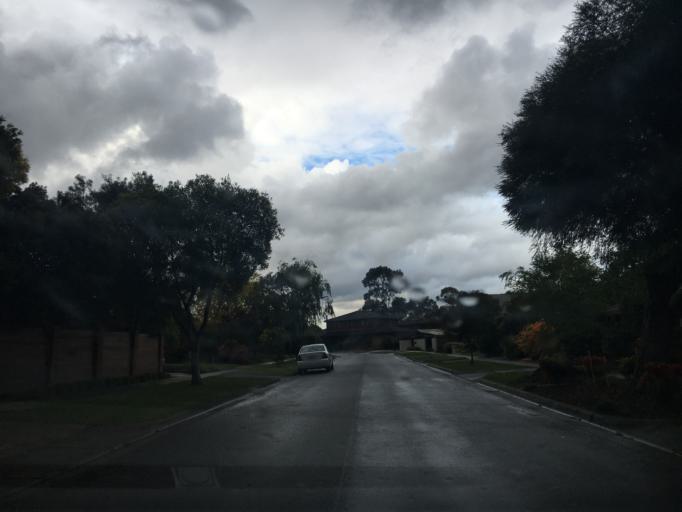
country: AU
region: Victoria
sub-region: Knox
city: Wantirna South
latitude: -37.8869
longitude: 145.1883
